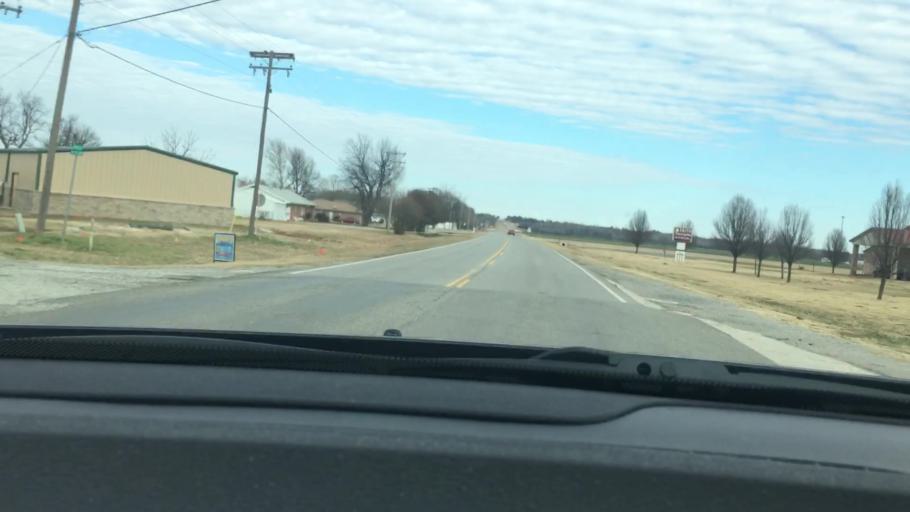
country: US
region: Oklahoma
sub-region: Garvin County
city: Pauls Valley
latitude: 34.7488
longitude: -97.2107
